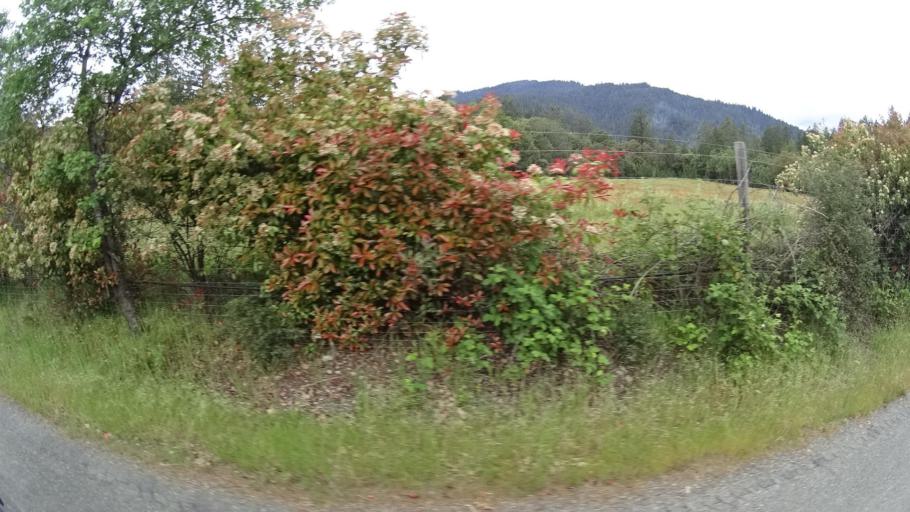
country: US
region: California
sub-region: Humboldt County
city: Willow Creek
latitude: 40.9605
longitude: -123.6303
